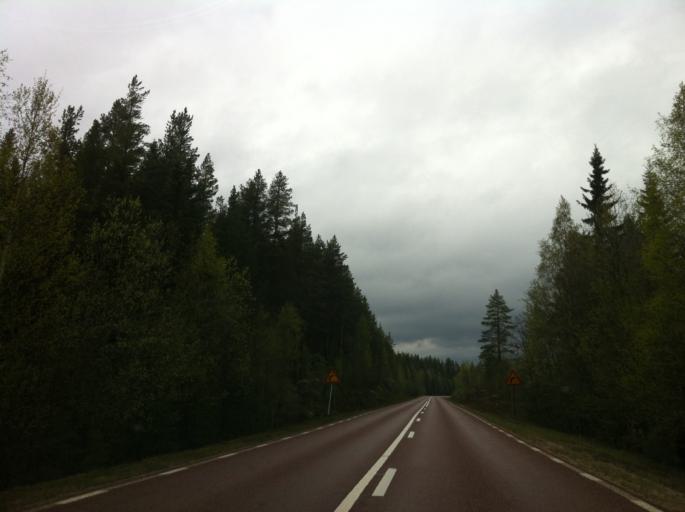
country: SE
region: Jaemtland
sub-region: Harjedalens Kommun
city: Sveg
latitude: 61.8883
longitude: 14.6248
